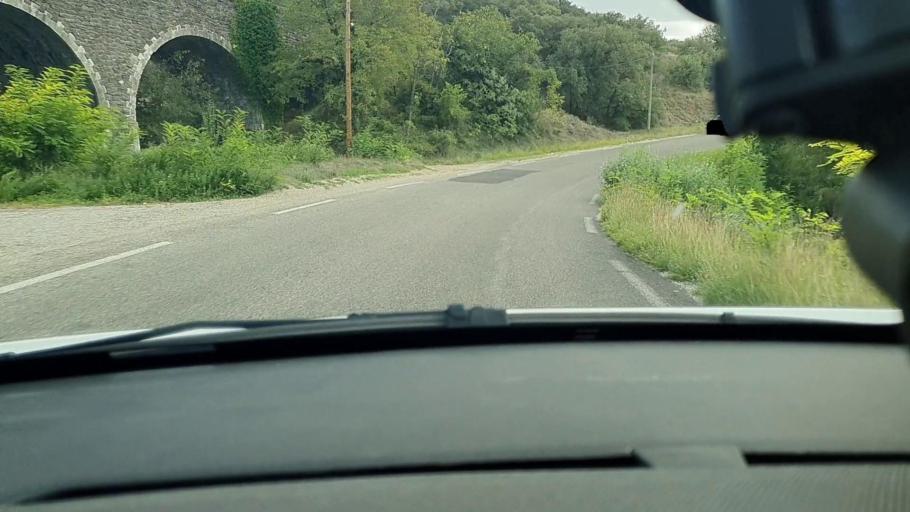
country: FR
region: Languedoc-Roussillon
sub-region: Departement du Gard
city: Les Mages
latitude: 44.2214
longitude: 4.1742
